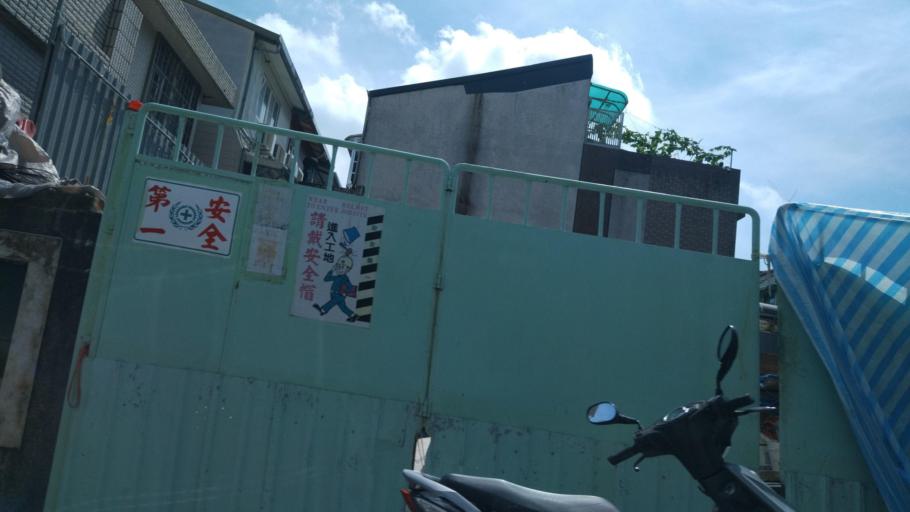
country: TW
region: Taipei
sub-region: Taipei
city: Banqiao
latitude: 24.9468
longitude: 121.4989
